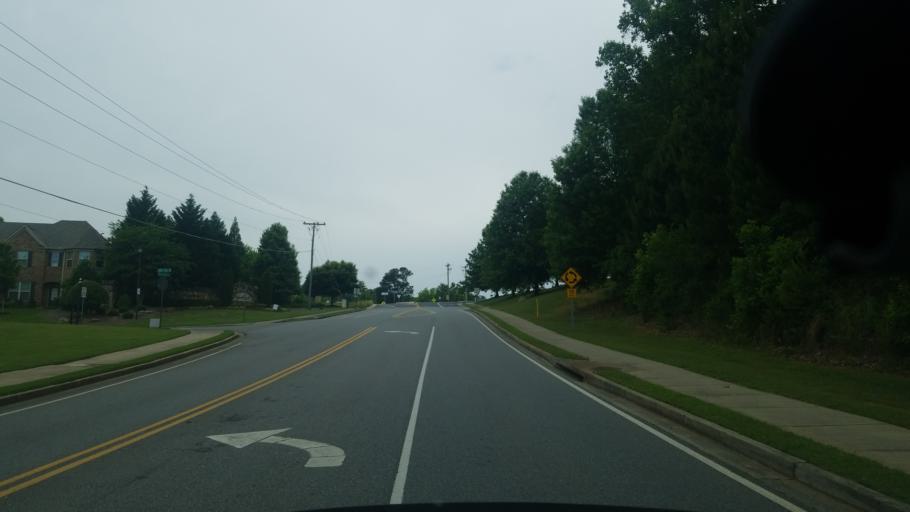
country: US
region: Georgia
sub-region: Forsyth County
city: Cumming
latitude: 34.1330
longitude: -84.1392
